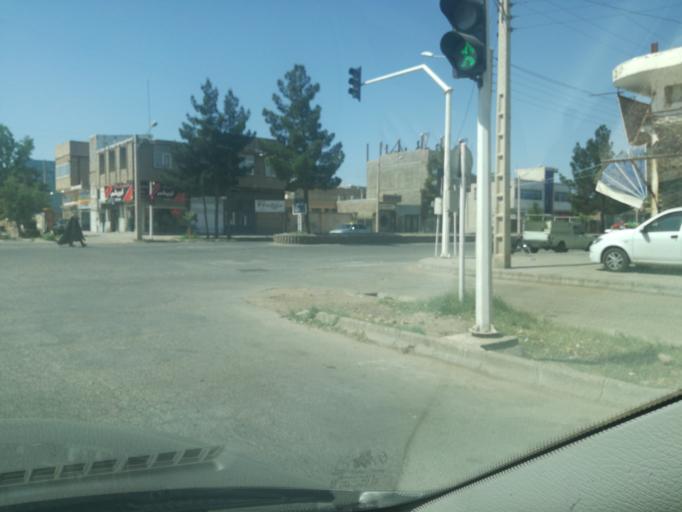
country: IR
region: Razavi Khorasan
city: Sarakhs
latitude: 36.5458
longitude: 61.1642
